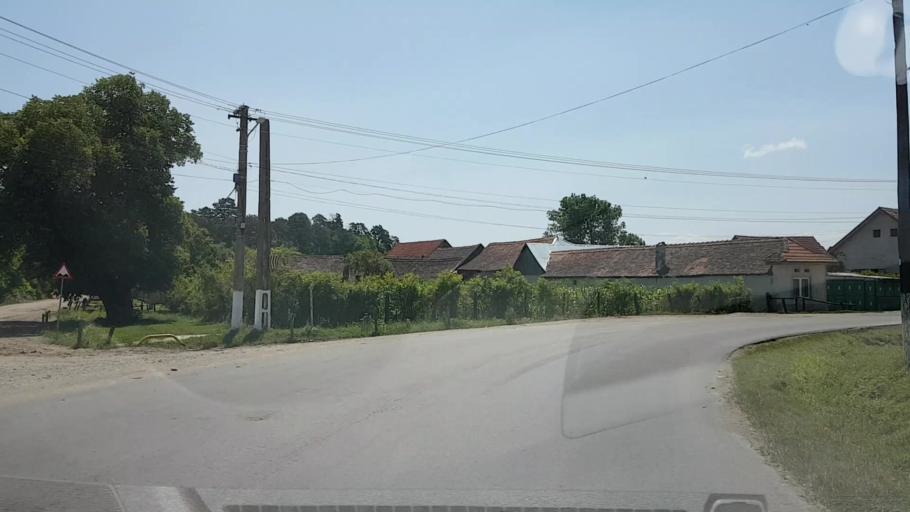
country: RO
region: Brasov
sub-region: Comuna Cincu
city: Cincu
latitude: 45.9175
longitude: 24.8087
